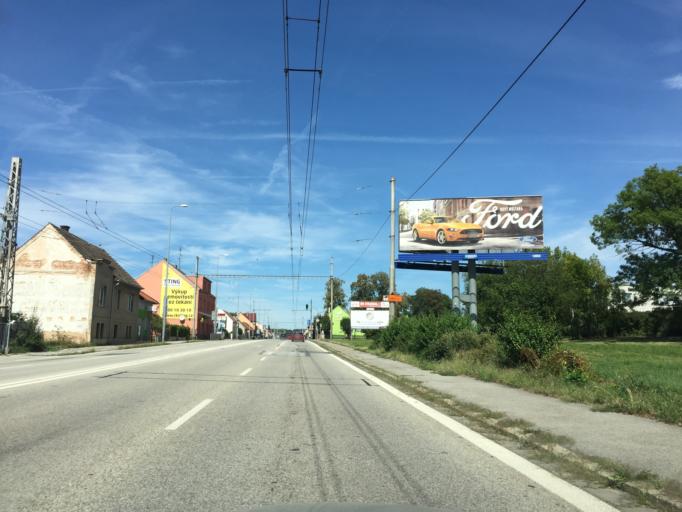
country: CZ
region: Jihocesky
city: Hrdejovice
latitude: 49.0048
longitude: 14.4864
